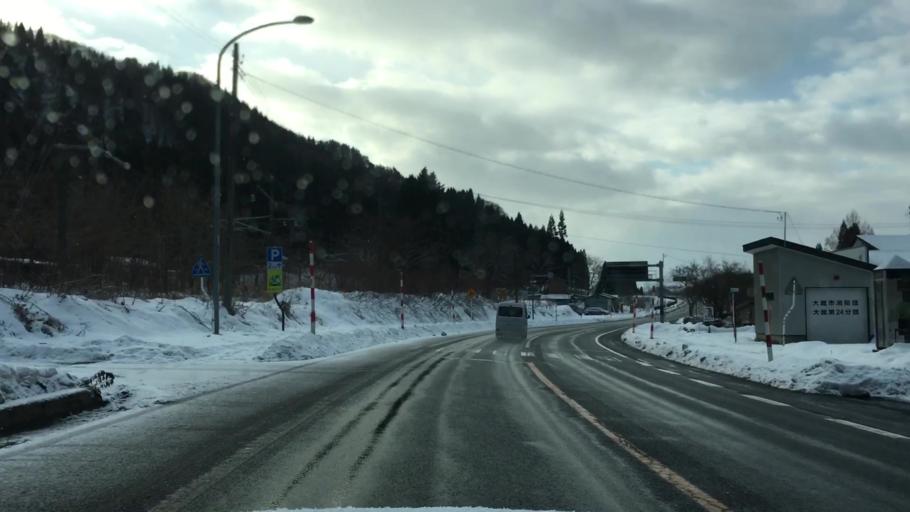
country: JP
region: Akita
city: Odate
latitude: 40.3997
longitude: 140.6068
